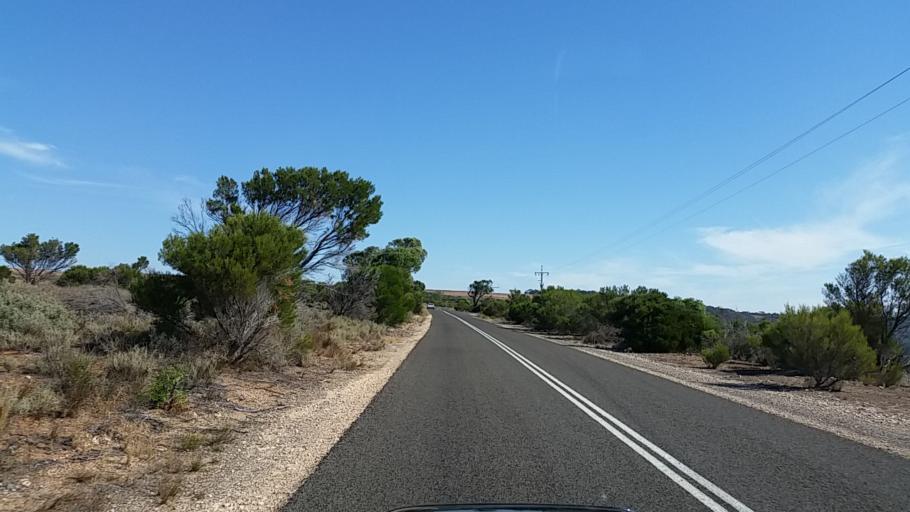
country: AU
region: South Australia
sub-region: Mid Murray
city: Mannum
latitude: -34.7477
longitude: 139.5452
